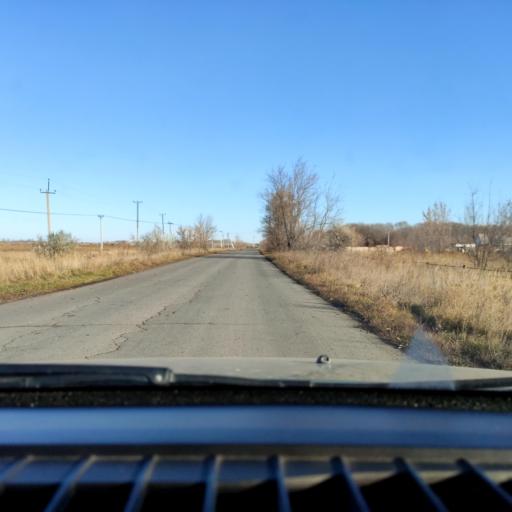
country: RU
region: Samara
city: Tol'yatti
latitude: 53.6464
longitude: 49.3189
